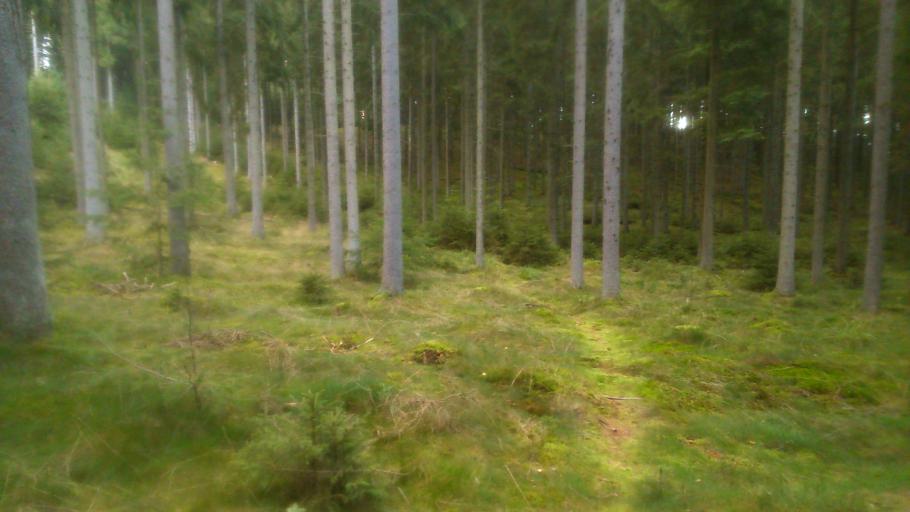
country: DK
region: Central Jutland
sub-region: Silkeborg Kommune
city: Svejbaek
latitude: 56.1569
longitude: 9.6146
